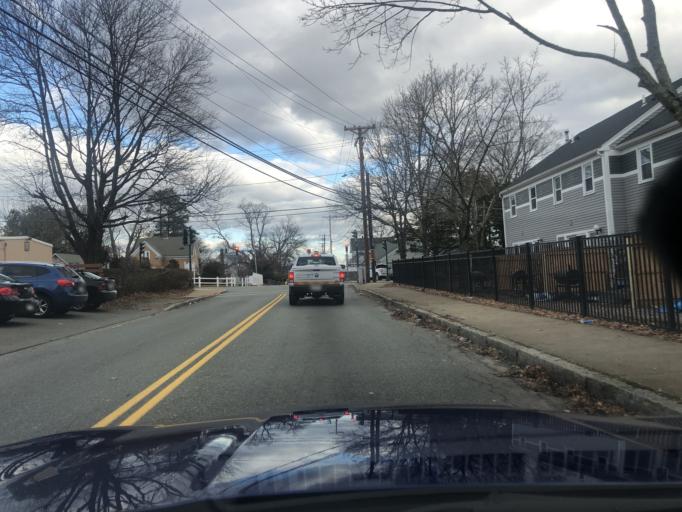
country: US
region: Massachusetts
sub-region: Plymouth County
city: Brockton
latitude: 42.0914
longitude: -71.0262
